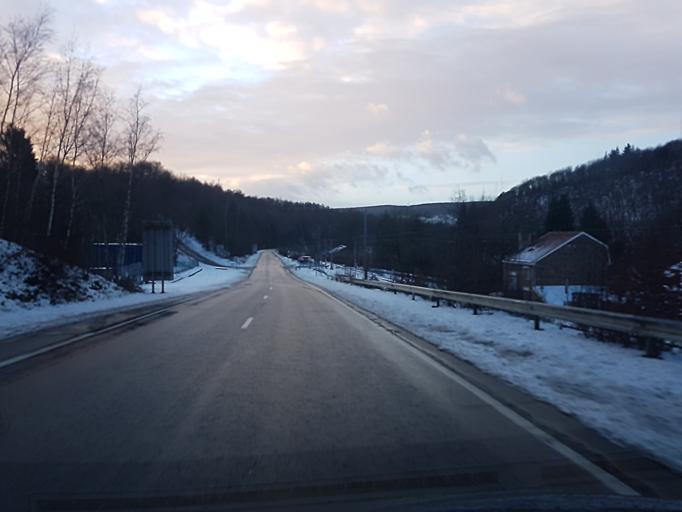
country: BE
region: Wallonia
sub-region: Province de Liege
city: Spa
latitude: 50.4881
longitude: 5.8434
